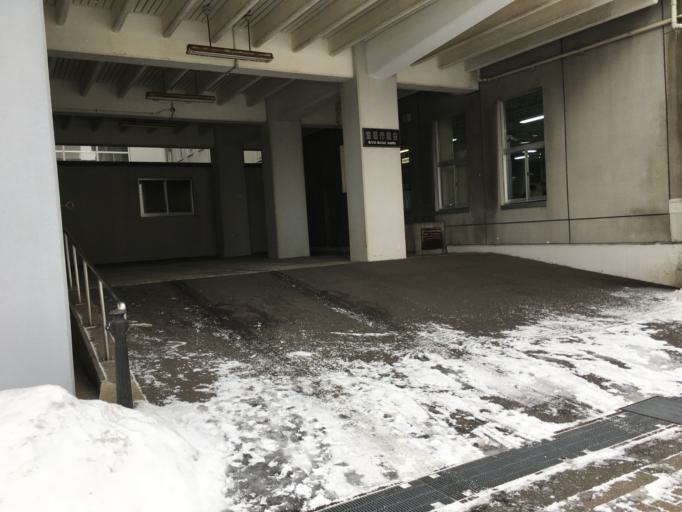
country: JP
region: Hokkaido
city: Muroran
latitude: 42.3153
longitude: 140.9739
